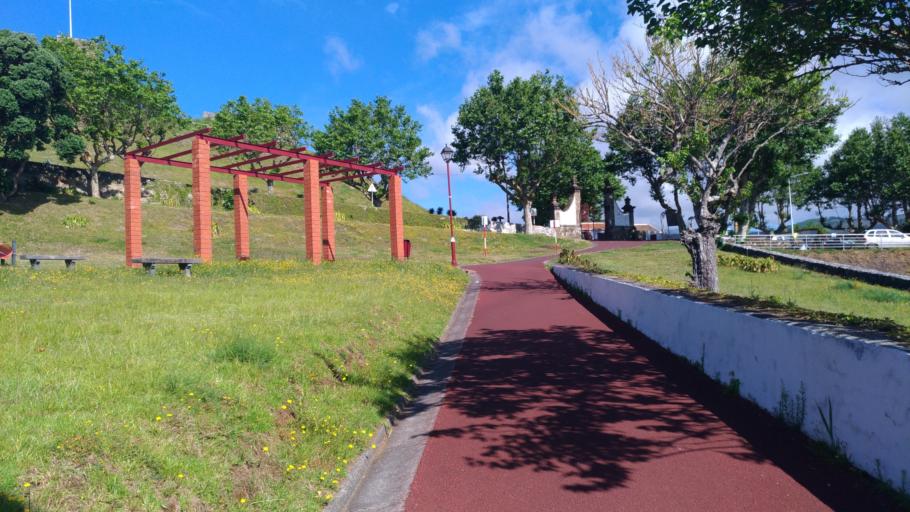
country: PT
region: Azores
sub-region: Angra do Heroismo
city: Angra do Heroismo
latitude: 38.6521
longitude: -27.2237
